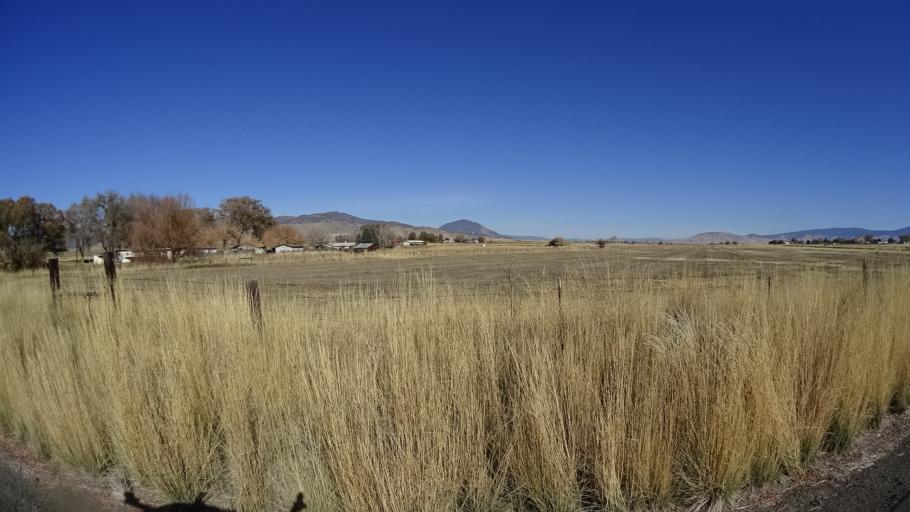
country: US
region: California
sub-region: Siskiyou County
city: Montague
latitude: 41.7348
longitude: -122.5232
